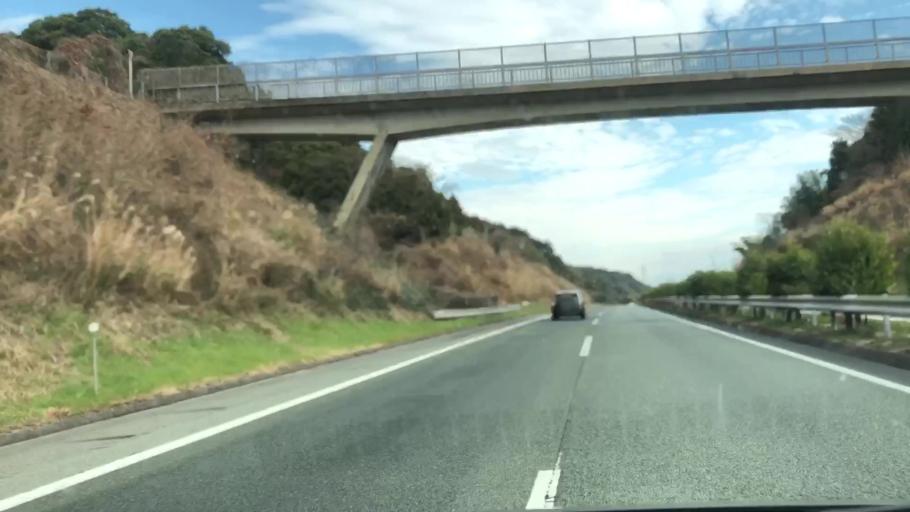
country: JP
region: Saga Prefecture
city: Tosu
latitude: 33.3913
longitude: 130.4909
